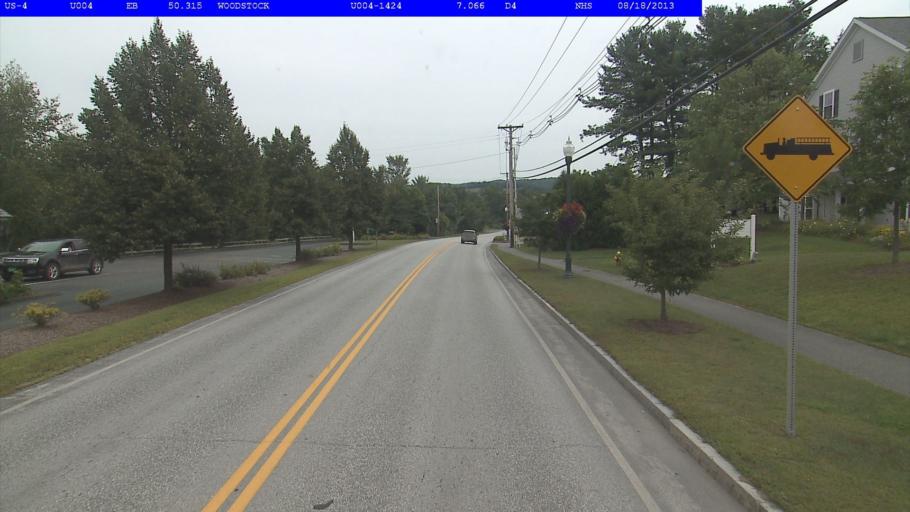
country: US
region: Vermont
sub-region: Windsor County
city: Woodstock
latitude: 43.6293
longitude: -72.5059
